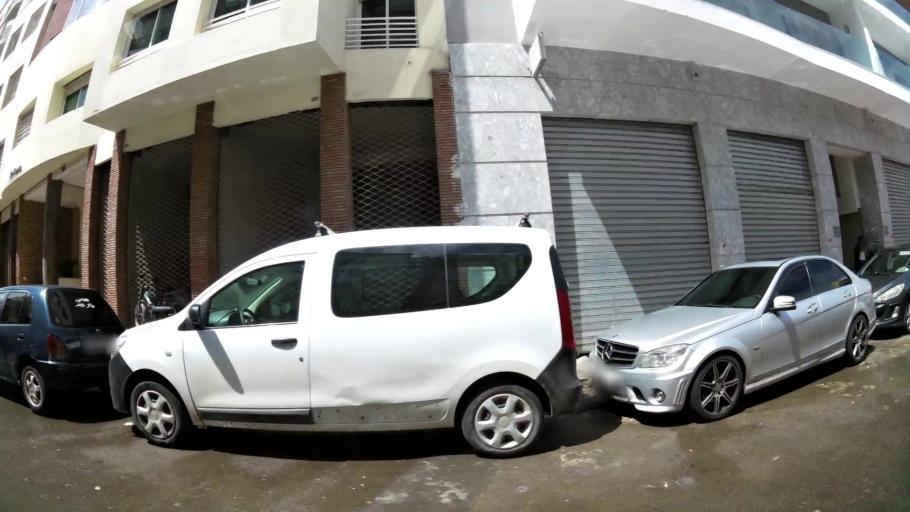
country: MA
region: Grand Casablanca
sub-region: Casablanca
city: Casablanca
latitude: 33.5738
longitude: -7.6379
